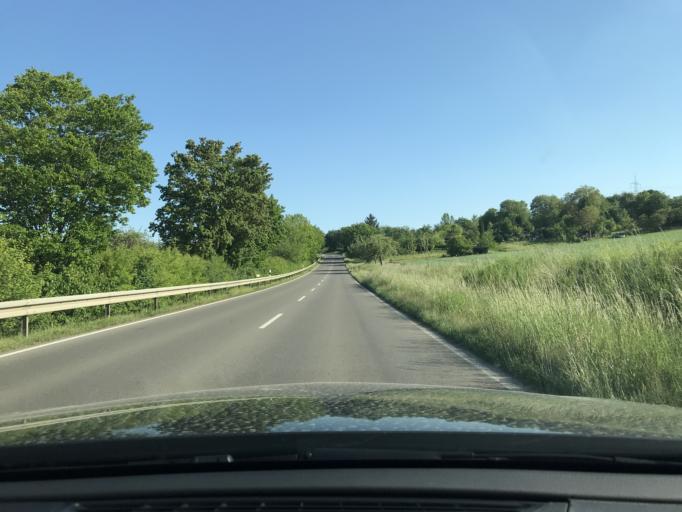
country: DE
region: Baden-Wuerttemberg
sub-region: Regierungsbezirk Stuttgart
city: Schwaikheim
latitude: 48.8804
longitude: 9.3178
